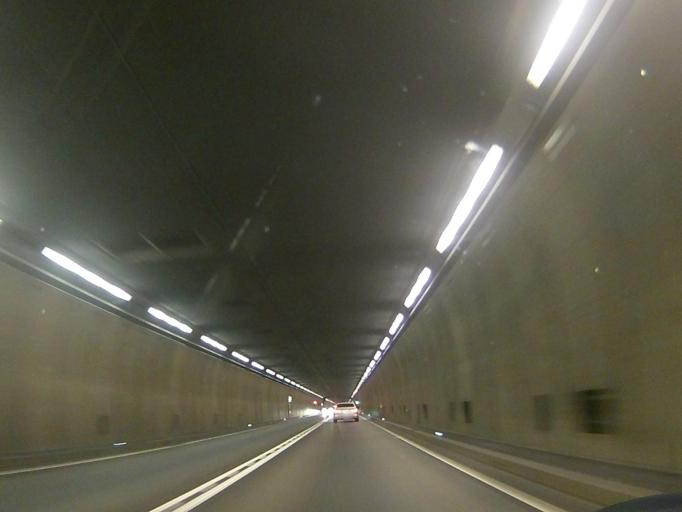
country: CH
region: Uri
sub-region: Uri
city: Andermatt
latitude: 46.6573
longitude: 8.5880
